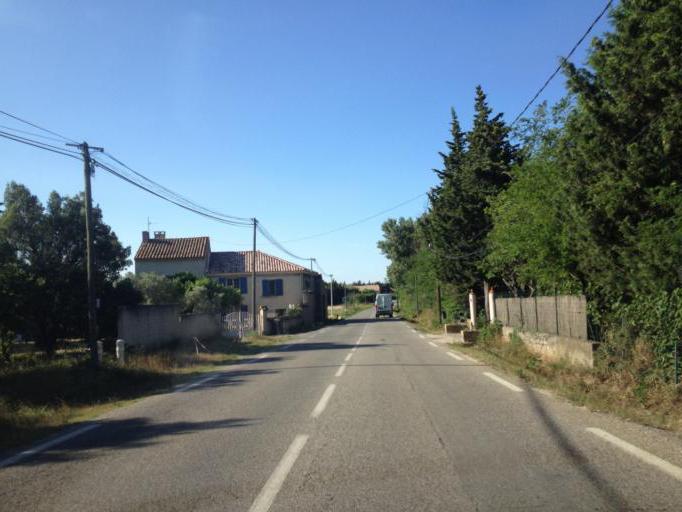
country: FR
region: Provence-Alpes-Cote d'Azur
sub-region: Departement du Vaucluse
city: Caderousse
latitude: 44.1055
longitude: 4.7912
